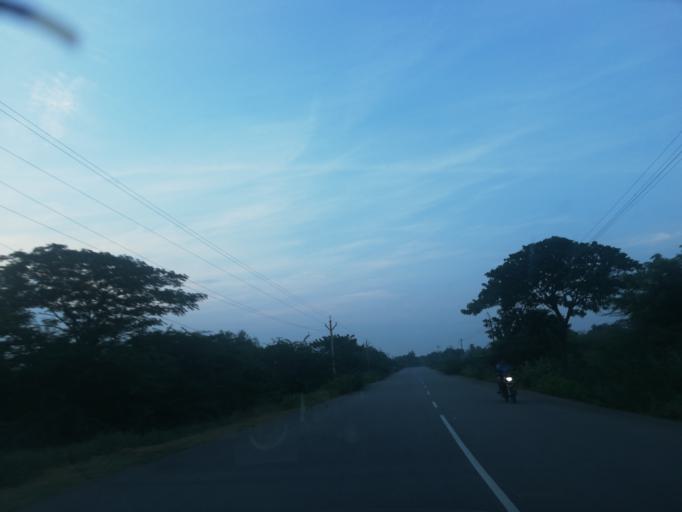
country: IN
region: Andhra Pradesh
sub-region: Guntur
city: Macherla
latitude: 16.5952
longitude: 79.3143
